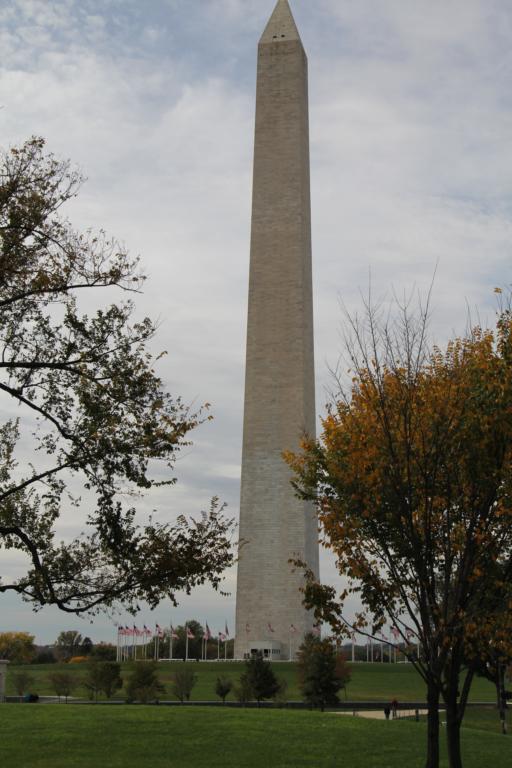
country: US
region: Washington, D.C.
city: Washington, D.C.
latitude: 38.8895
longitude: -77.0352
